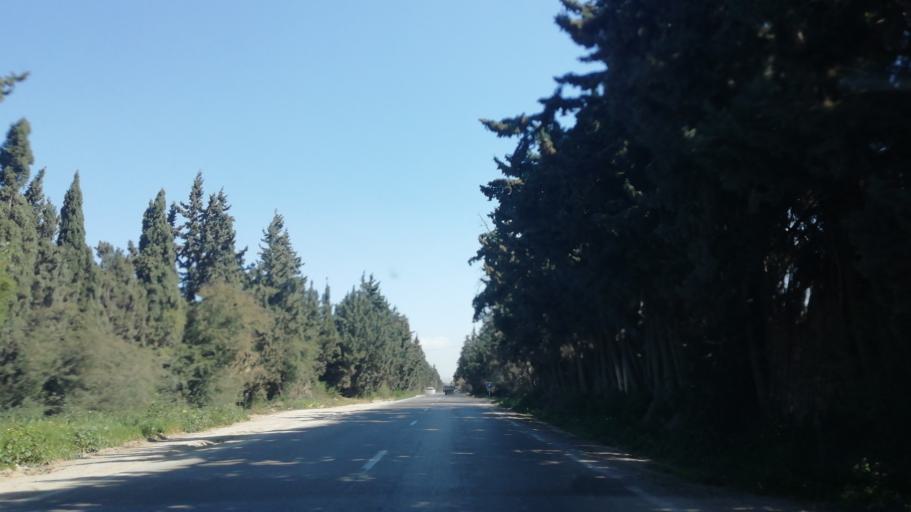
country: DZ
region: Mascara
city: Sig
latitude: 35.5787
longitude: 0.0108
